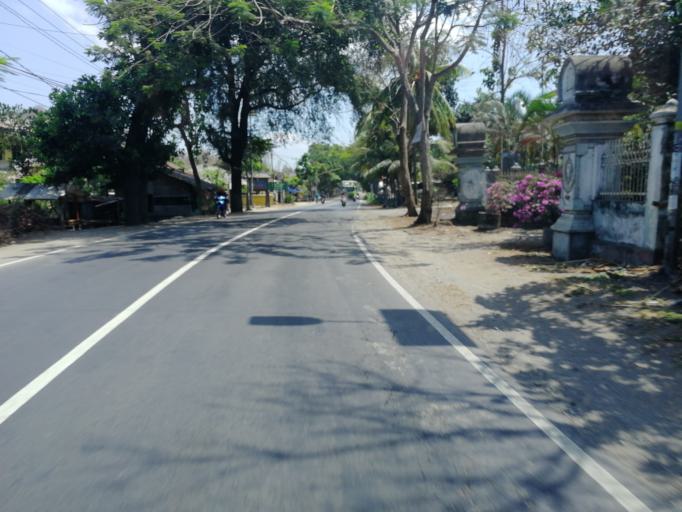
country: ID
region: West Nusa Tenggara
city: Jelateng Timur
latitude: -8.7181
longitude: 116.0738
